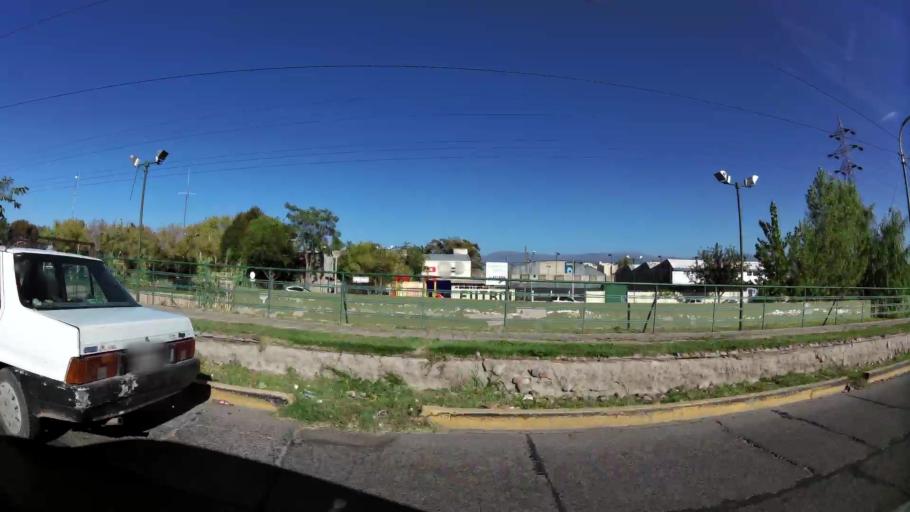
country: AR
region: Mendoza
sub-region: Departamento de Godoy Cruz
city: Godoy Cruz
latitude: -32.9376
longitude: -68.8410
